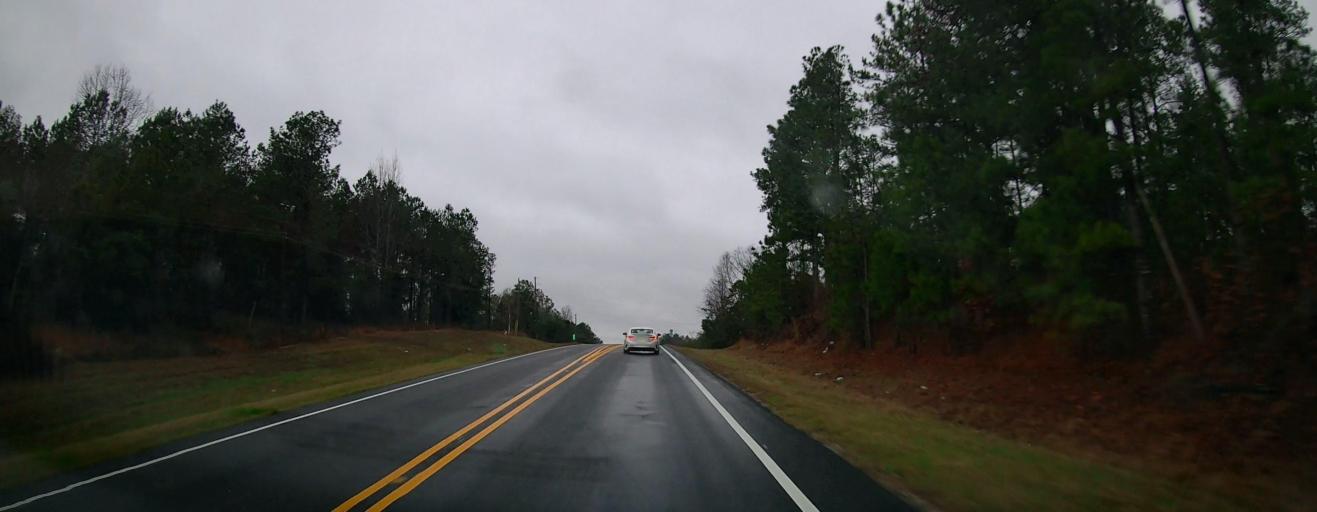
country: US
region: Alabama
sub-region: Chilton County
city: Clanton
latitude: 32.6890
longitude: -86.7941
